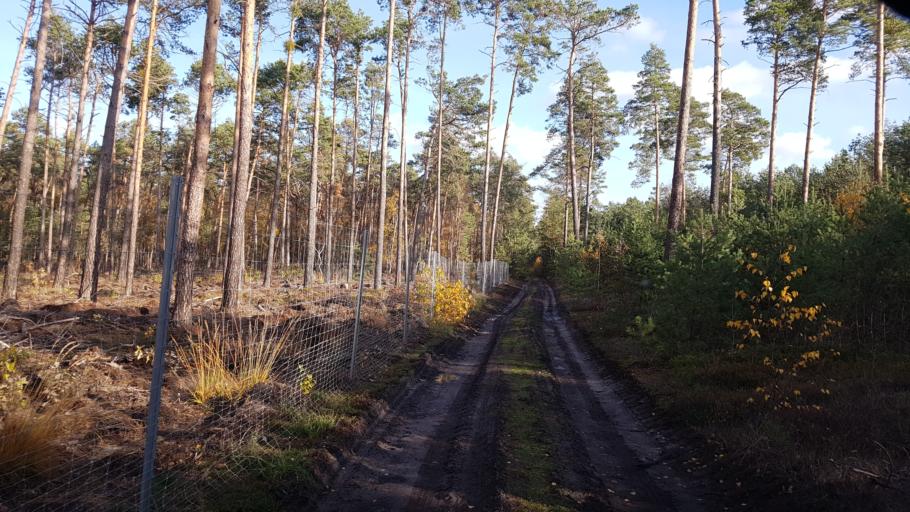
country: DE
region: Brandenburg
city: Trobitz
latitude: 51.6446
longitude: 13.4140
